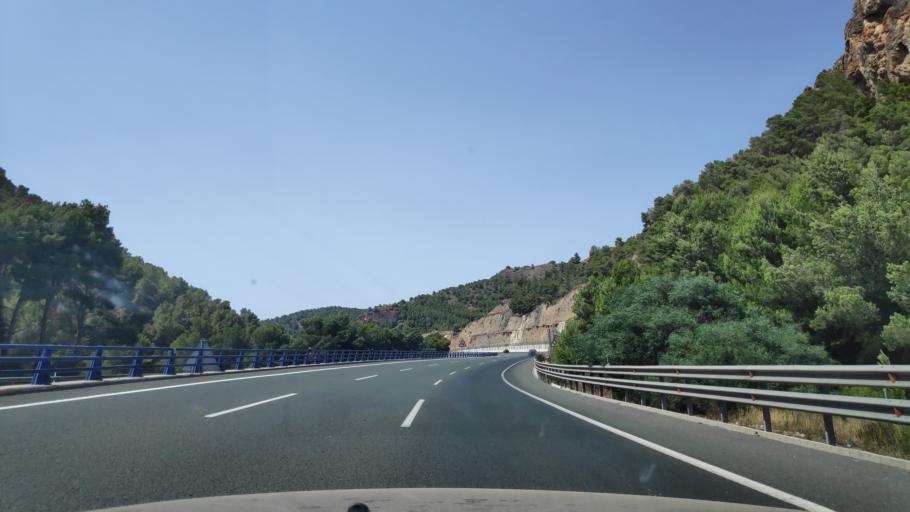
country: ES
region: Murcia
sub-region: Murcia
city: Murcia
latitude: 37.9000
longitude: -1.1426
